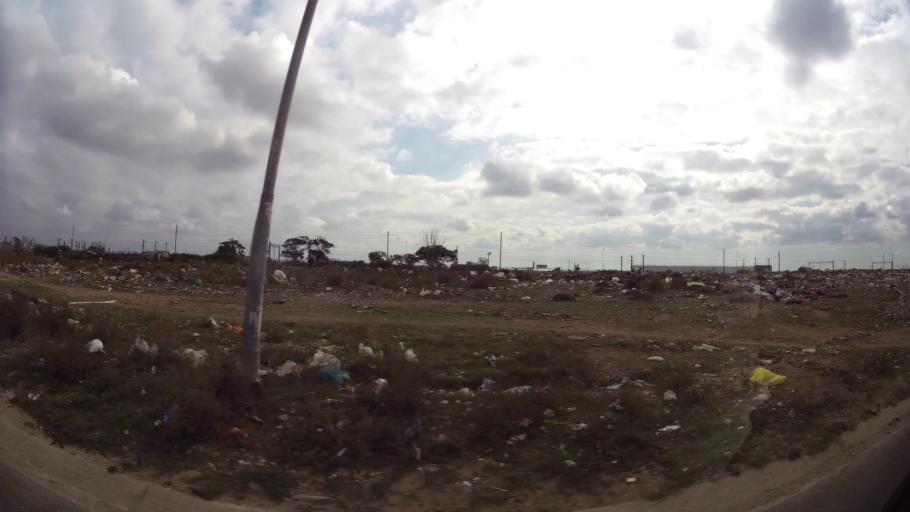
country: ZA
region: Eastern Cape
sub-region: Nelson Mandela Bay Metropolitan Municipality
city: Port Elizabeth
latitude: -33.8189
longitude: 25.6299
